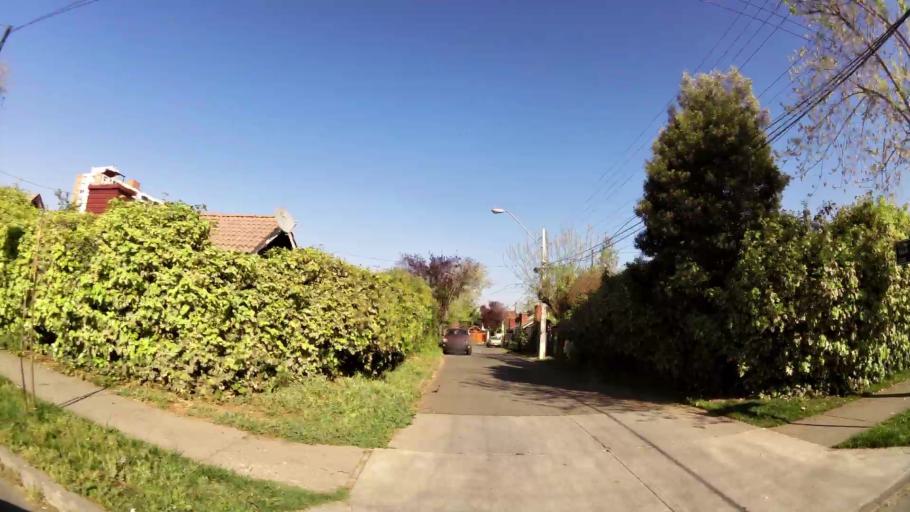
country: CL
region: Santiago Metropolitan
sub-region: Provincia de Santiago
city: Villa Presidente Frei, Nunoa, Santiago, Chile
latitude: -33.4414
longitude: -70.5751
